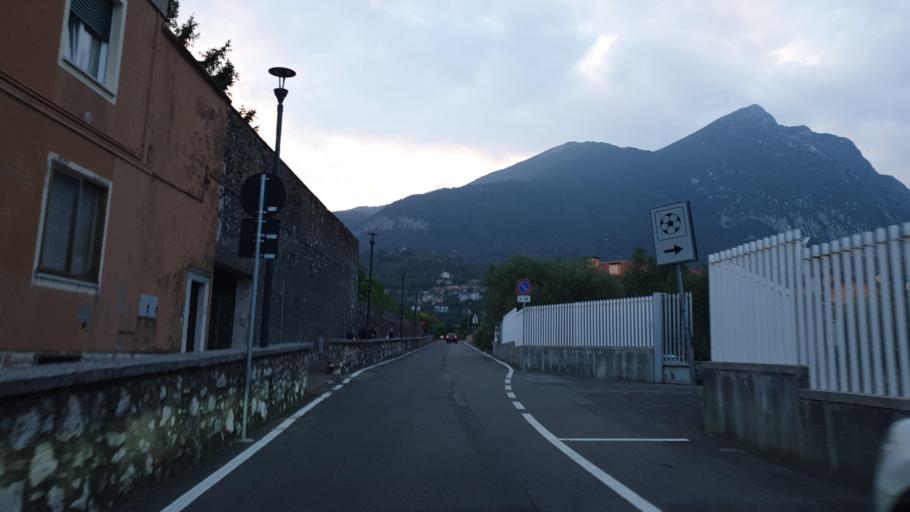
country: IT
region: Lombardy
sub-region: Provincia di Brescia
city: Toscolano Maderno
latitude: 45.6369
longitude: 10.6159
